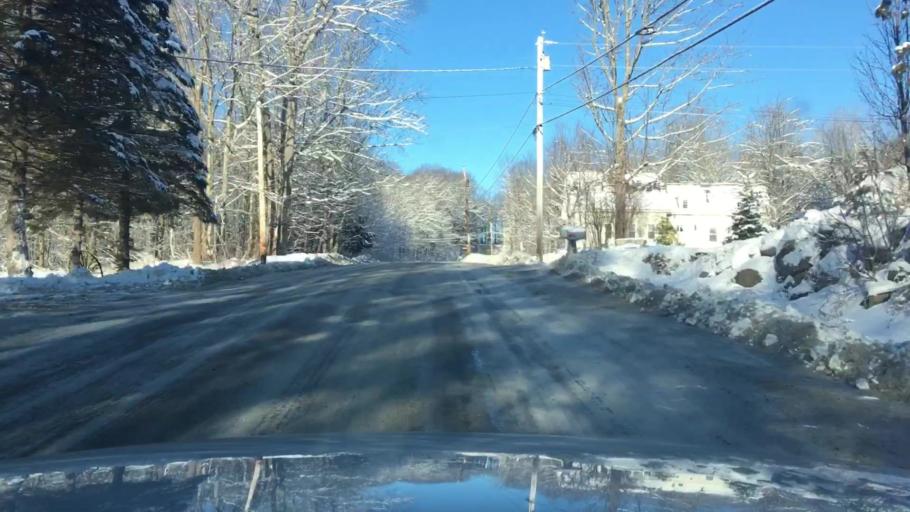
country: US
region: Maine
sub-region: Kennebec County
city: Readfield
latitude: 44.4193
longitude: -69.9250
